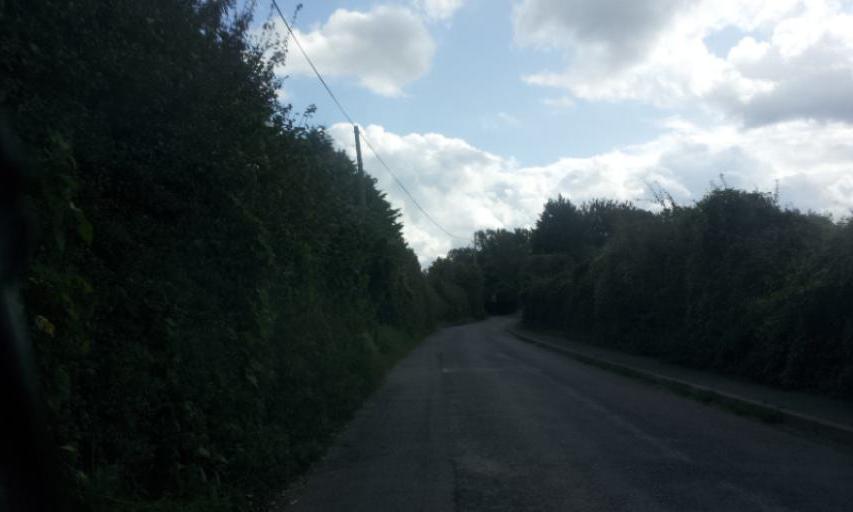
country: GB
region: England
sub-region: Kent
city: Newington
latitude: 51.3369
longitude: 0.6981
